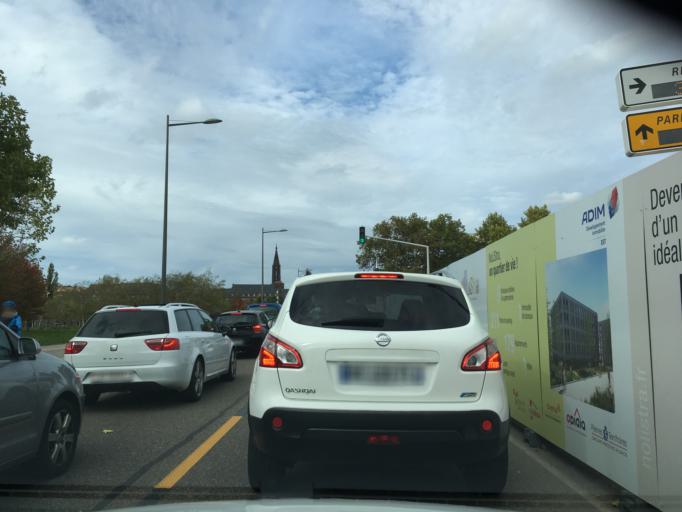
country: FR
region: Alsace
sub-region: Departement du Bas-Rhin
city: Strasbourg
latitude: 48.5726
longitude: 7.7558
